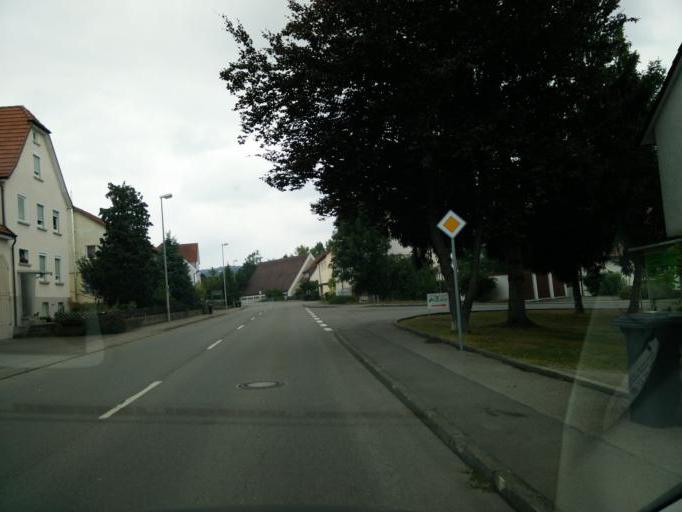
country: DE
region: Baden-Wuerttemberg
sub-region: Tuebingen Region
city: Gomaringen
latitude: 48.4514
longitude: 9.0902
